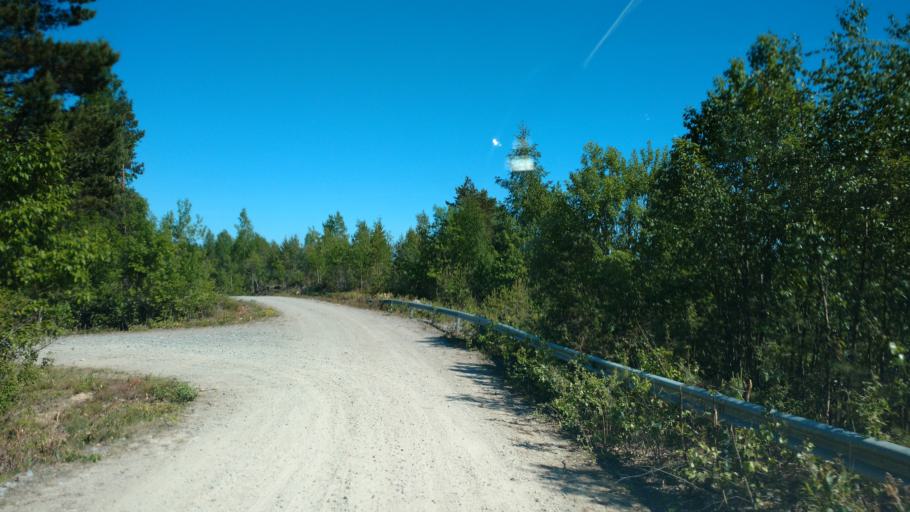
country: FI
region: Varsinais-Suomi
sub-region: Salo
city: Halikko
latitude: 60.4351
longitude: 22.9721
